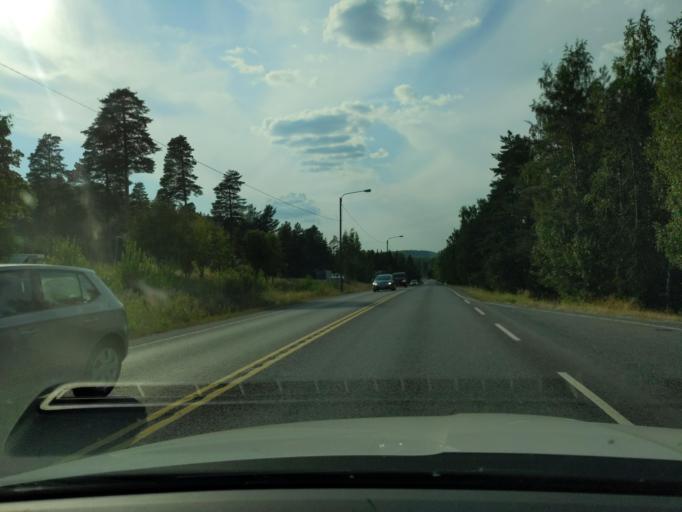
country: FI
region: Paijanne Tavastia
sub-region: Lahti
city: Asikkala
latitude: 61.1659
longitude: 25.5650
